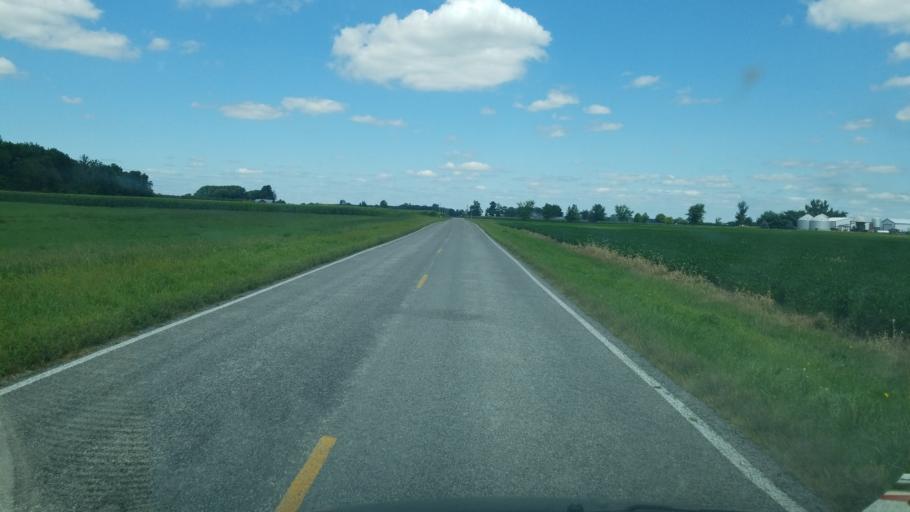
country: US
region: Ohio
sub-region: Fulton County
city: Delta
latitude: 41.6089
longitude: -84.0084
